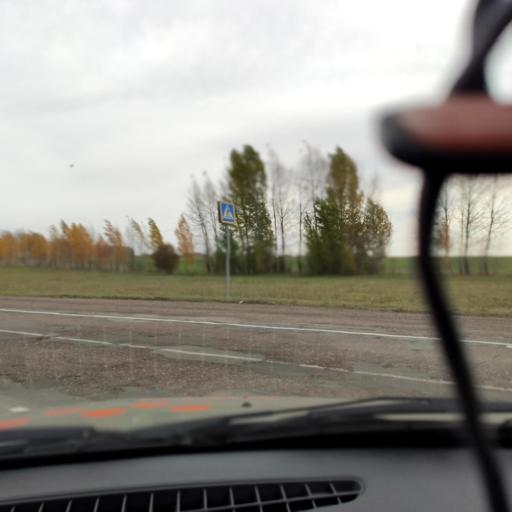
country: RU
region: Bashkortostan
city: Kabakovo
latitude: 54.5219
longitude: 56.0258
